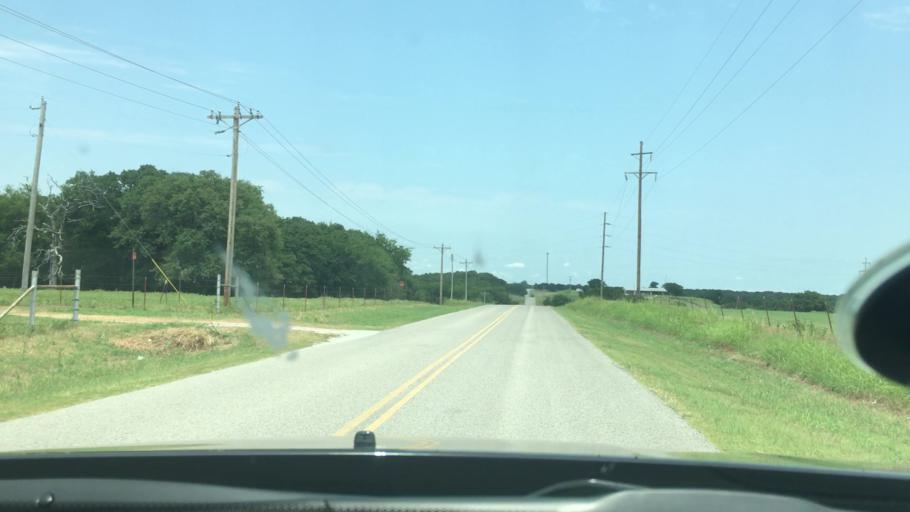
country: US
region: Oklahoma
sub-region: Love County
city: Marietta
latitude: 33.9223
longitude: -97.3521
